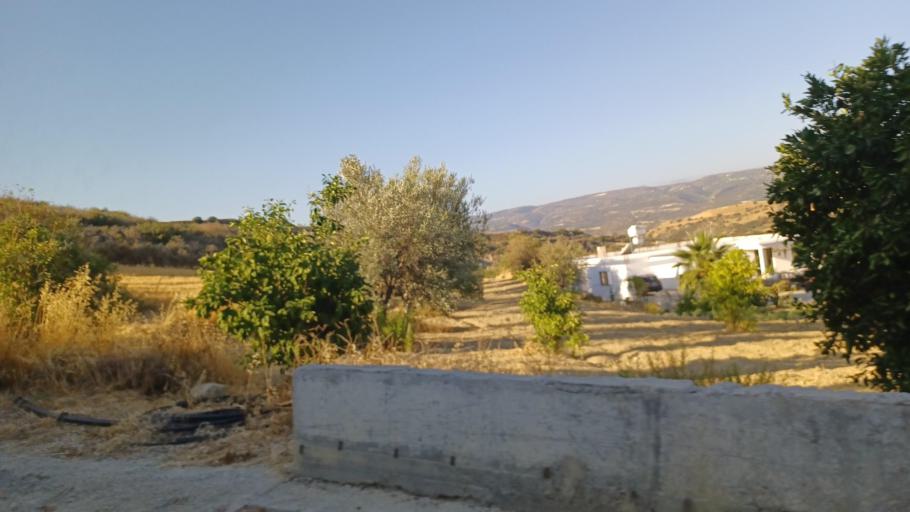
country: CY
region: Pafos
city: Polis
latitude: 34.9956
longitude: 32.4696
